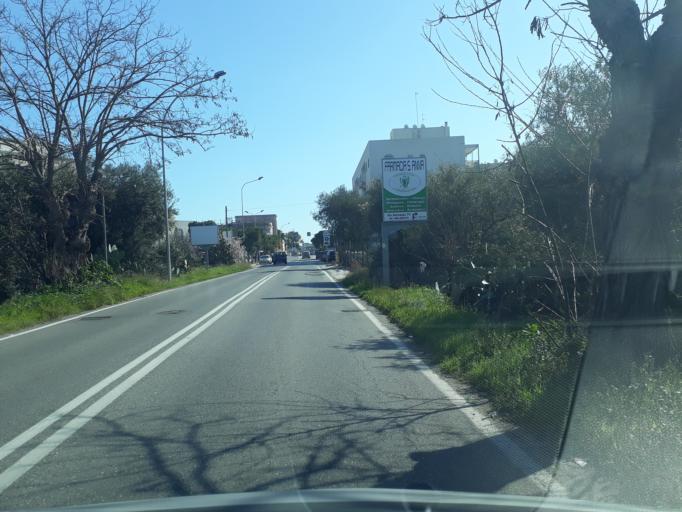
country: IT
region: Apulia
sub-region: Provincia di Bari
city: Monopoli
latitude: 40.9518
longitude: 17.2865
